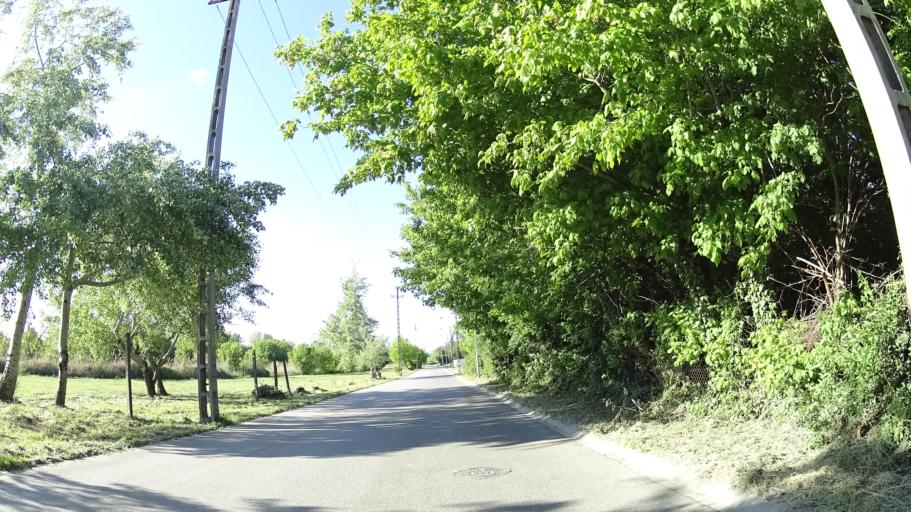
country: HU
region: Budapest
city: Budapest XXIII. keruelet
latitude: 47.3960
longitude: 19.1117
